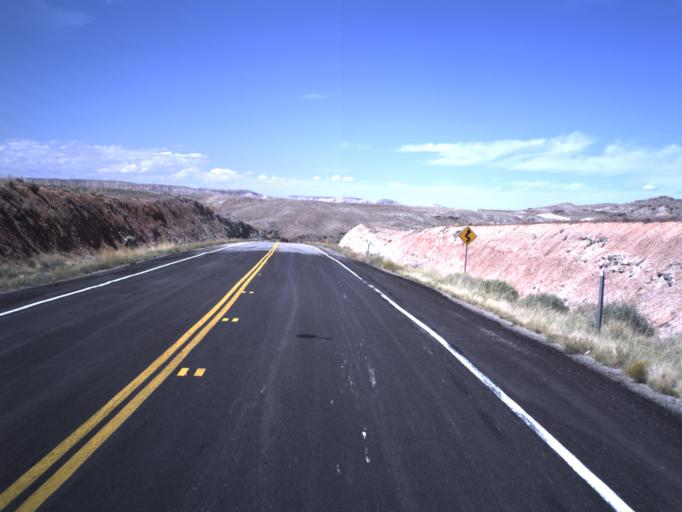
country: US
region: Colorado
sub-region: Montezuma County
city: Towaoc
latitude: 37.1719
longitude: -109.0933
